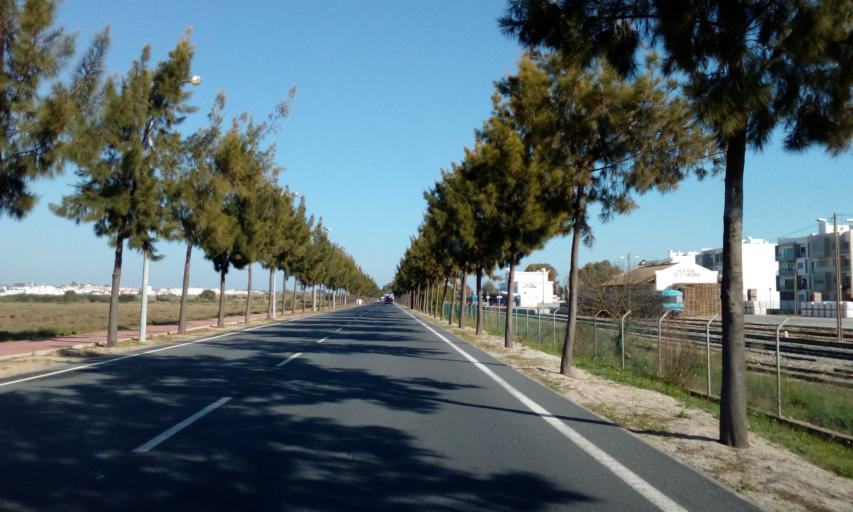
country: PT
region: Faro
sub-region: Vila Real de Santo Antonio
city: Vila Real de Santo Antonio
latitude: 37.1988
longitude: -7.4238
